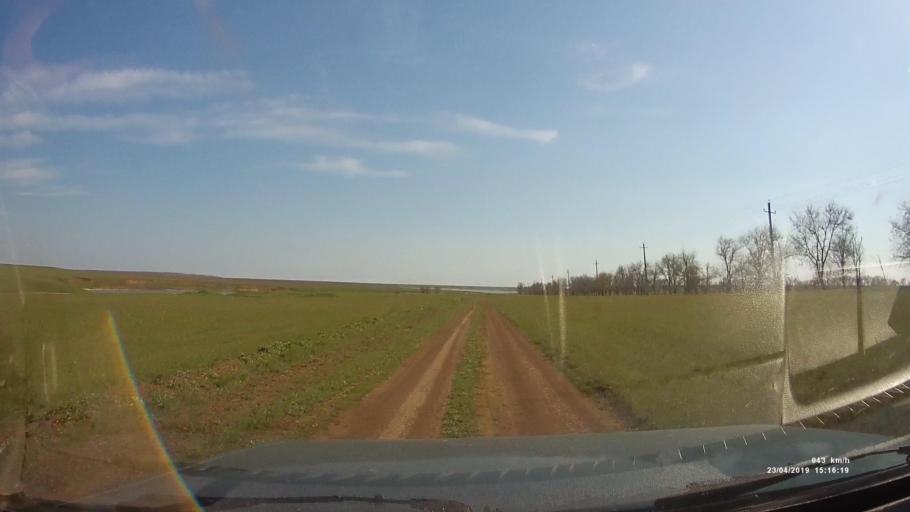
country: RU
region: Rostov
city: Remontnoye
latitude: 46.5343
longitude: 42.9698
